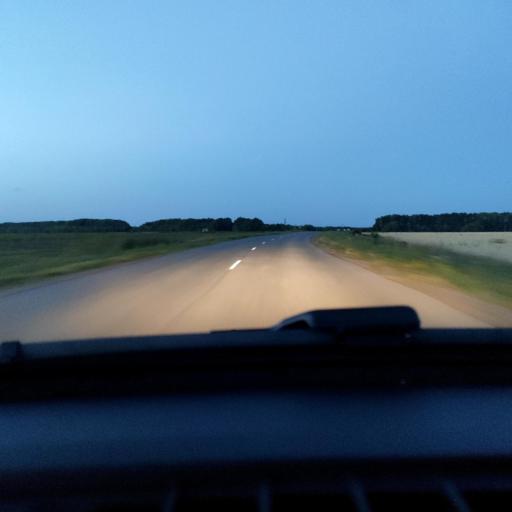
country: RU
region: Lipetsk
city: Zadonsk
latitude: 52.2983
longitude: 38.7934
